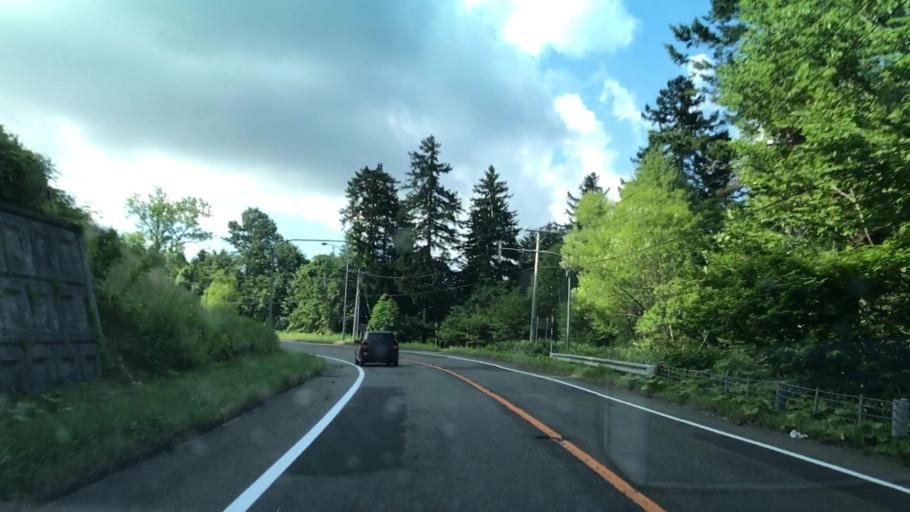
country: JP
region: Hokkaido
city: Shimo-furano
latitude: 42.9115
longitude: 142.4110
